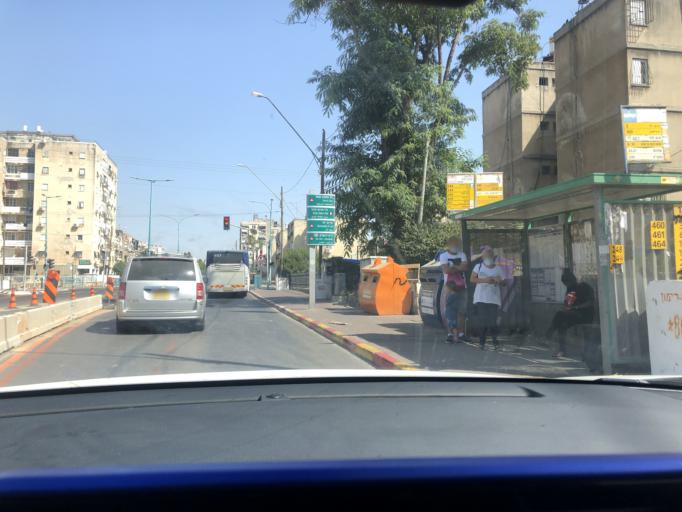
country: IL
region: Central District
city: Lod
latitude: 31.9500
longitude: 34.8876
